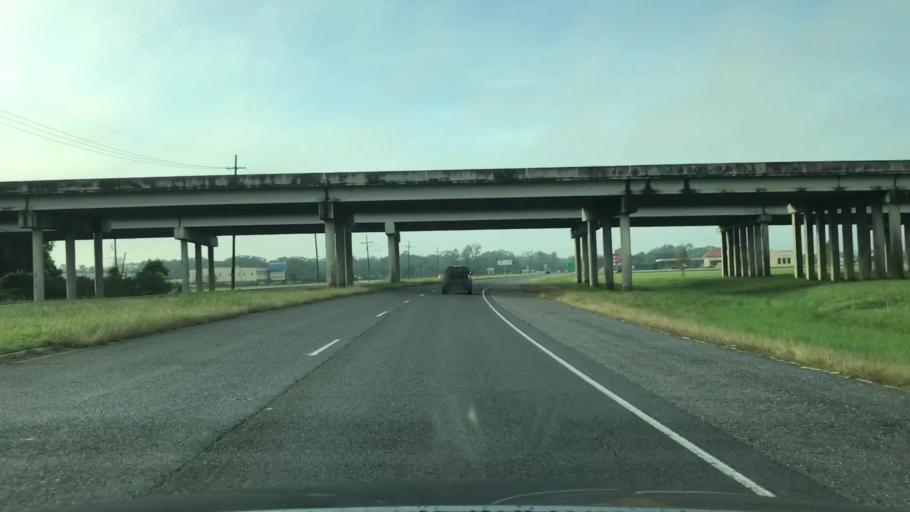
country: US
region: Louisiana
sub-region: Terrebonne Parish
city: Gray
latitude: 29.6823
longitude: -90.8117
